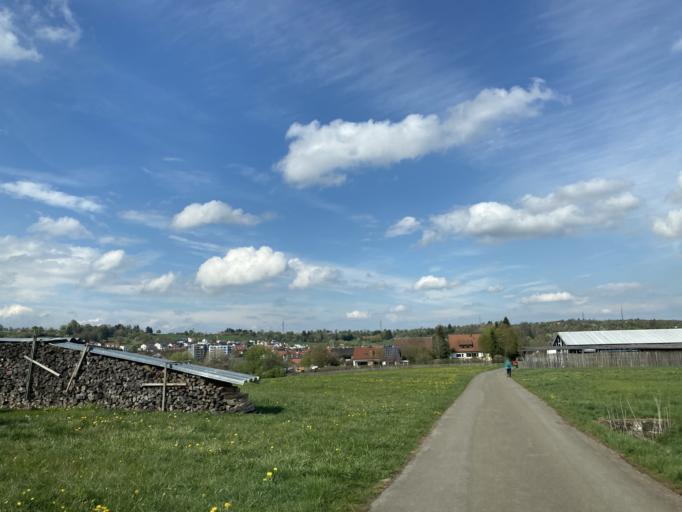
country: DE
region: Baden-Wuerttemberg
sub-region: Tuebingen Region
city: Dettenhausen
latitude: 48.6047
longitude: 9.0908
